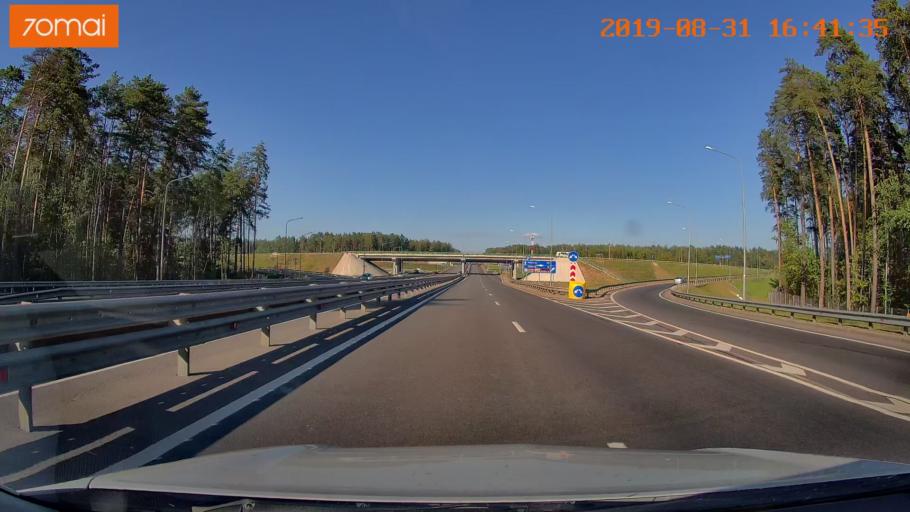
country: RU
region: Kaluga
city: Mstikhino
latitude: 54.5821
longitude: 36.0698
